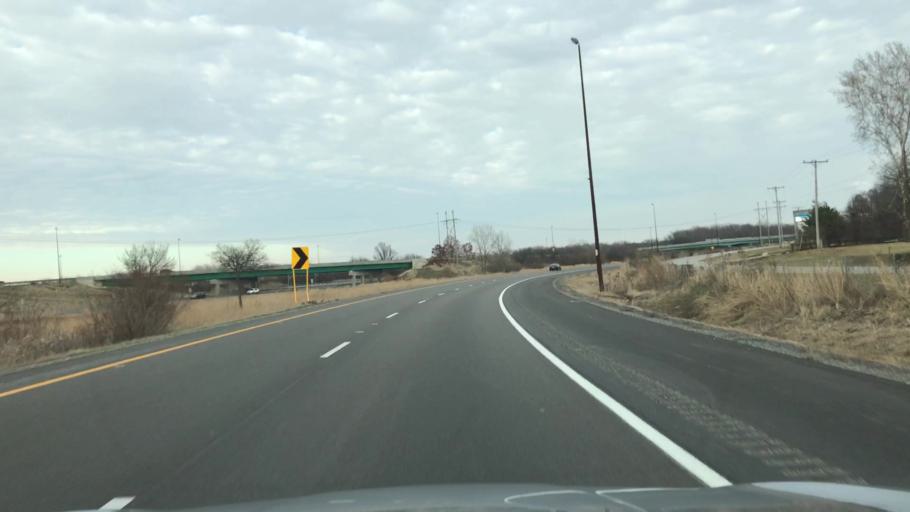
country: US
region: Illinois
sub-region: Sangamon County
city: Southern View
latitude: 39.7406
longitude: -89.6414
